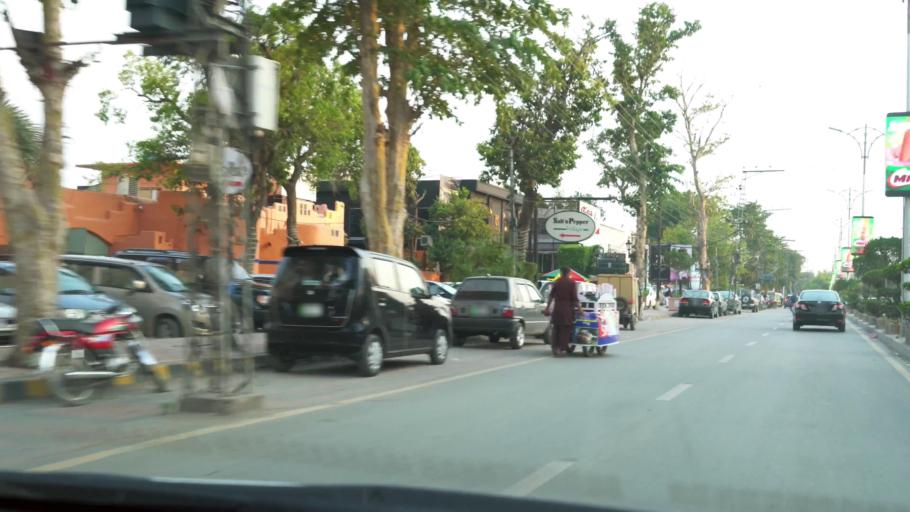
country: PK
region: Punjab
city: Lahore
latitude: 31.5107
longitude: 74.3507
